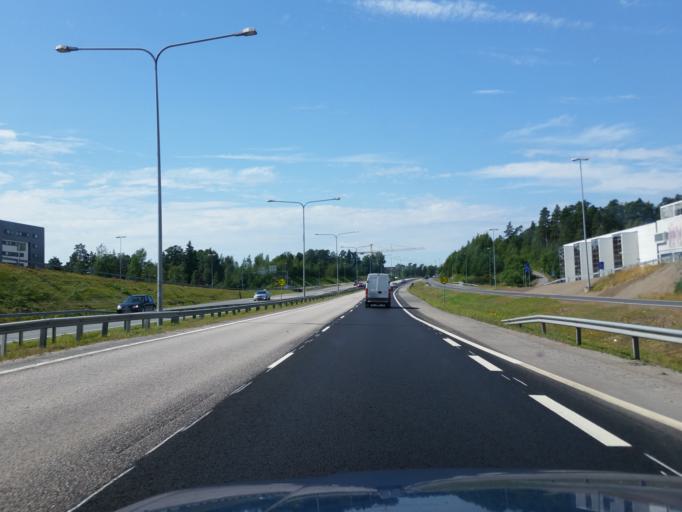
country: FI
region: Uusimaa
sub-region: Helsinki
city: Koukkuniemi
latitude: 60.1637
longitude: 24.7374
